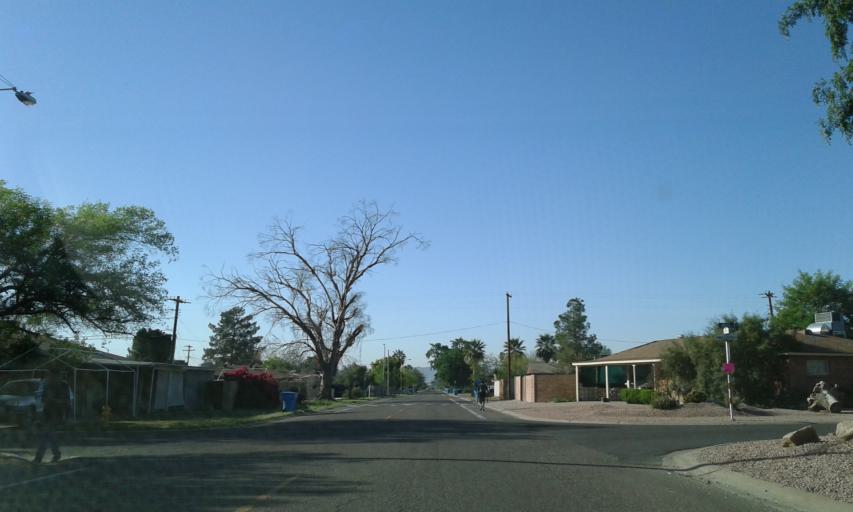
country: US
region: Arizona
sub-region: Maricopa County
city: Phoenix
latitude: 33.4908
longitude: -112.1084
